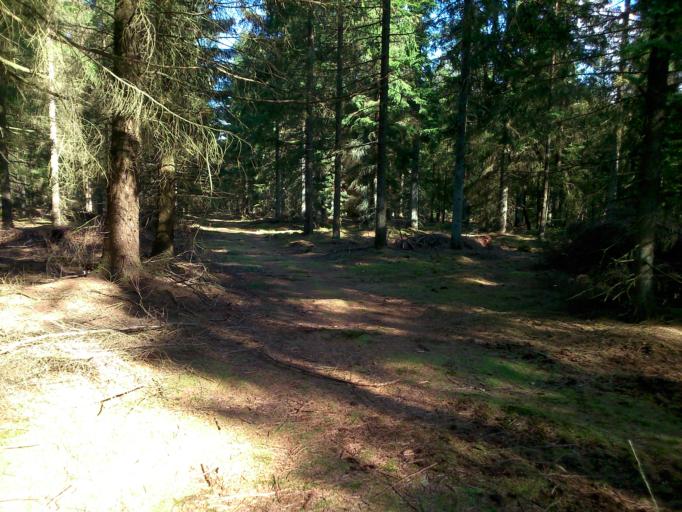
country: DK
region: Central Jutland
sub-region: Ringkobing-Skjern Kommune
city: Tarm
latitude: 55.9025
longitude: 8.5457
